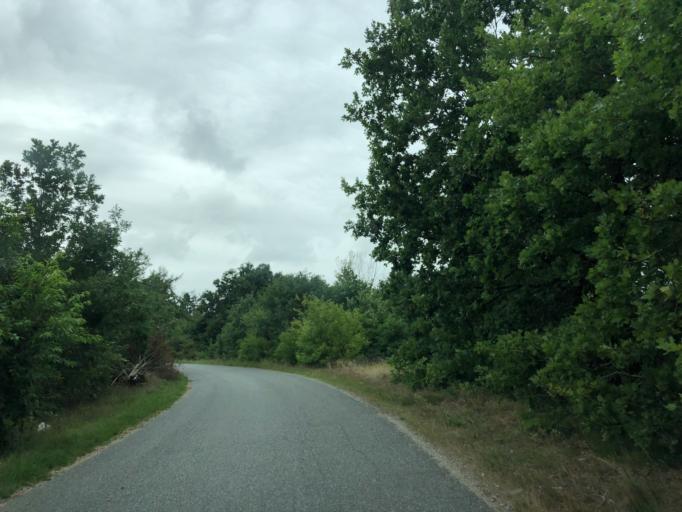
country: DK
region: Central Jutland
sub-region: Herning Kommune
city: Lind
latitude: 56.0766
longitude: 8.9672
